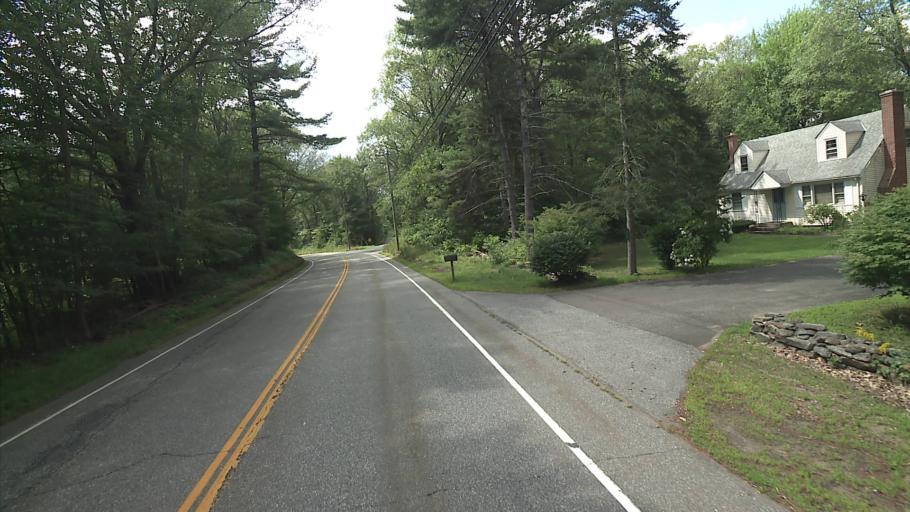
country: US
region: Massachusetts
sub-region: Hampden County
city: Holland
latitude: 41.9881
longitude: -72.1664
